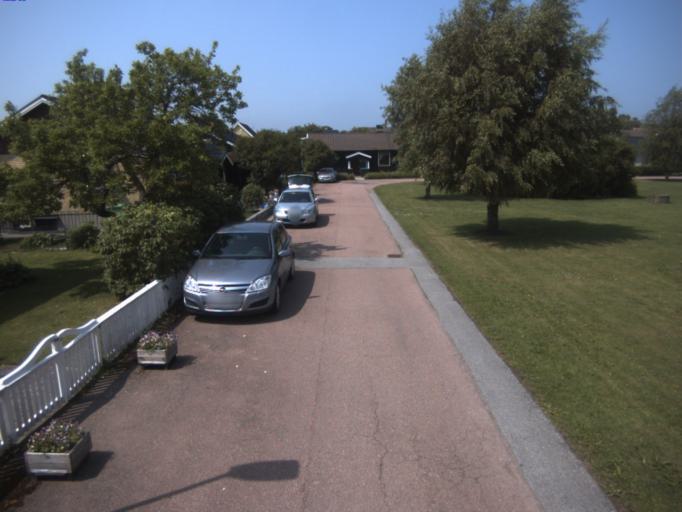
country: SE
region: Skane
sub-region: Angelholms Kommun
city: Strovelstorp
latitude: 56.2147
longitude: 12.7827
